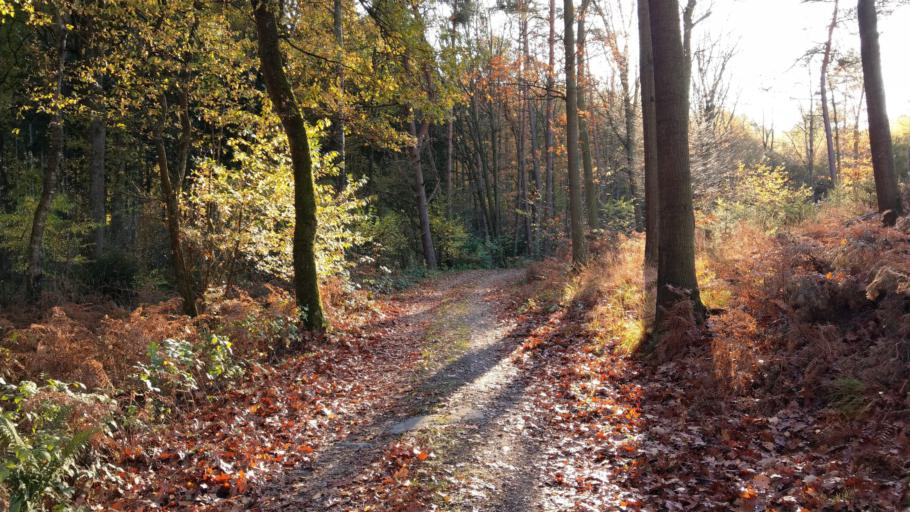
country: BE
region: Wallonia
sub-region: Province de Liege
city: La Calamine
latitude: 50.7341
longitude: 6.0289
